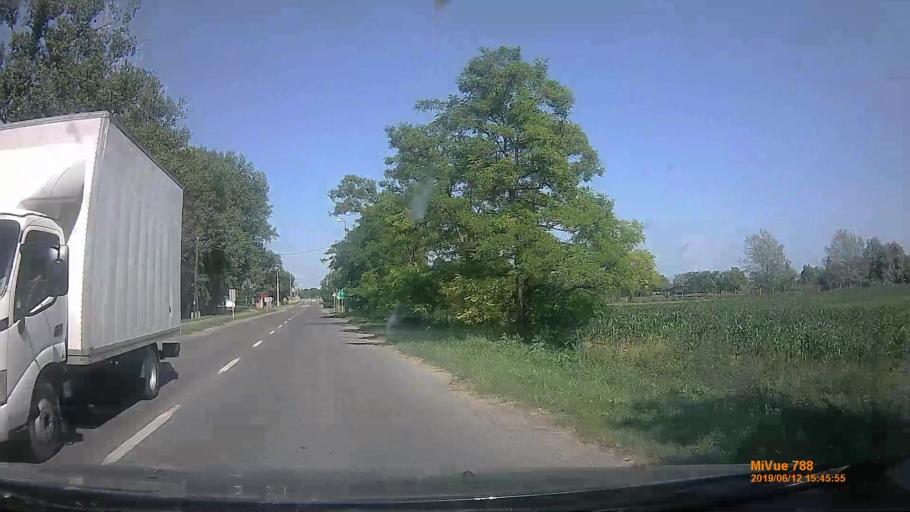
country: HU
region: Csongrad
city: Mako
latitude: 46.2169
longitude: 20.5155
